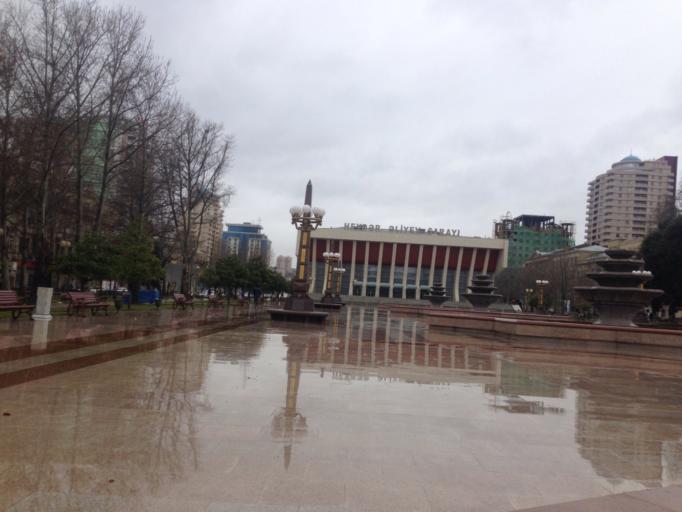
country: AZ
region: Baki
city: Baku
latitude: 40.3782
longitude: 49.8440
